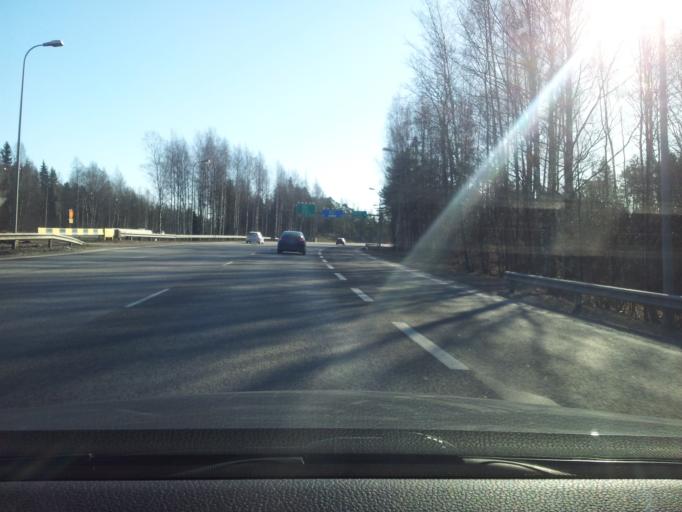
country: FI
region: Uusimaa
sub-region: Helsinki
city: Vantaa
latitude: 60.2409
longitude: 25.0323
